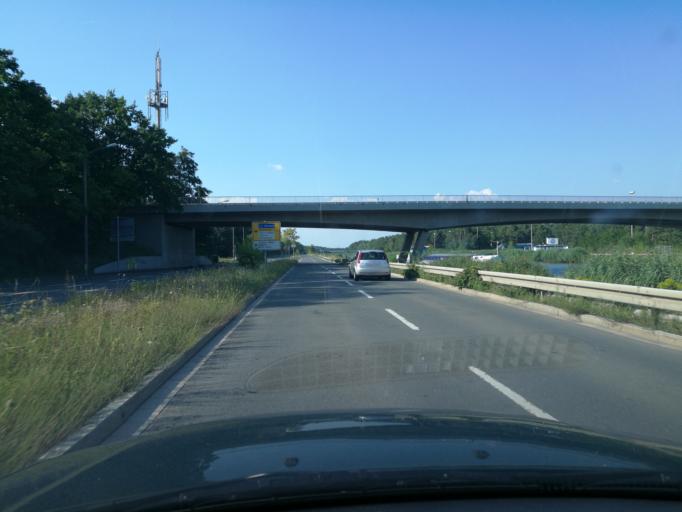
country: DE
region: Bavaria
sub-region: Regierungsbezirk Mittelfranken
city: Erlangen
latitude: 49.6007
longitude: 10.9716
